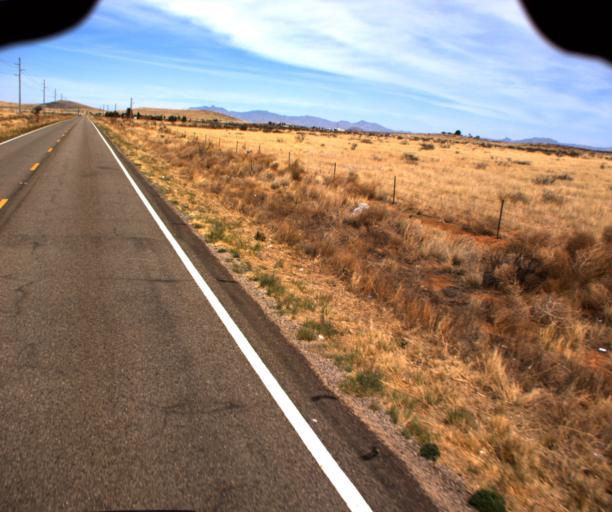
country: US
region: Arizona
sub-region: Cochise County
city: Tombstone
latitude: 31.8673
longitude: -109.6951
